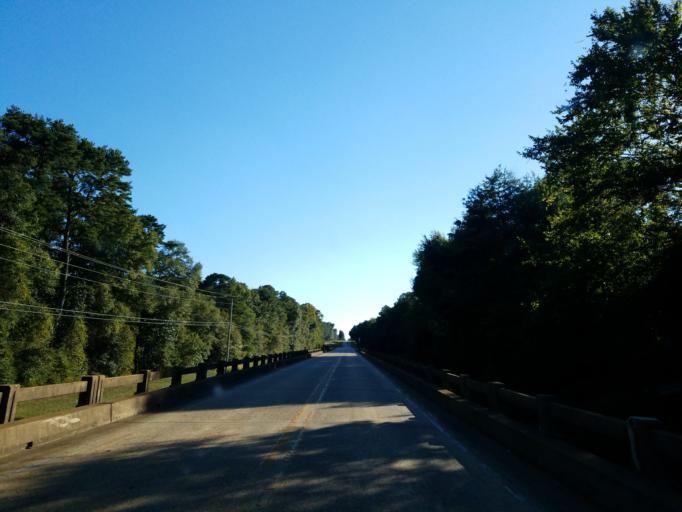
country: US
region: Georgia
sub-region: Lee County
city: Leesburg
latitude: 31.7772
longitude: -84.1385
